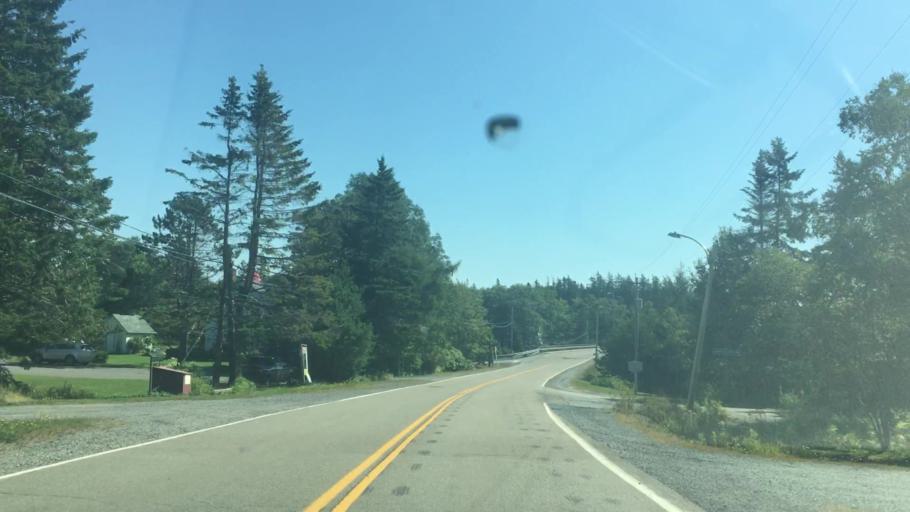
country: CA
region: Nova Scotia
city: Antigonish
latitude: 45.1441
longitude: -61.9858
